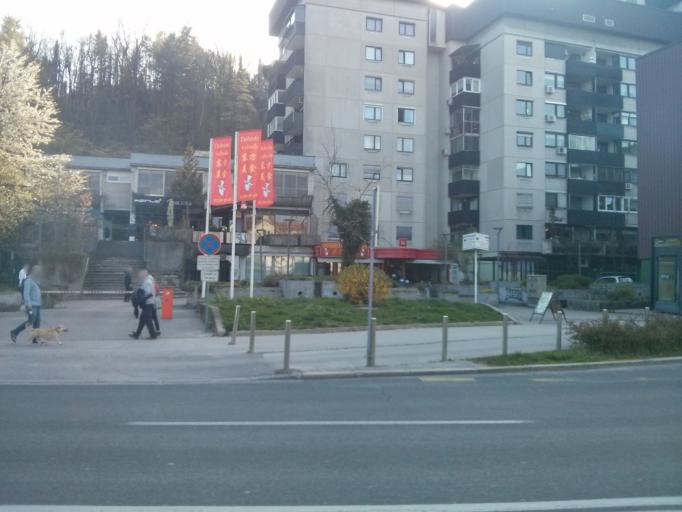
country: SI
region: Ljubljana
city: Ljubljana
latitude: 46.0637
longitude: 14.4945
